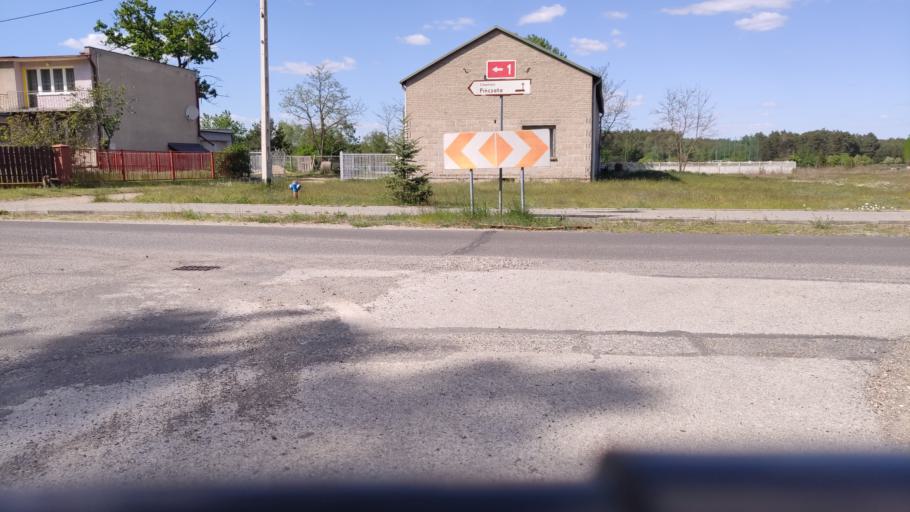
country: PL
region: Kujawsko-Pomorskie
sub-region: Wloclawek
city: Wloclawek
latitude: 52.6029
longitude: 19.0813
